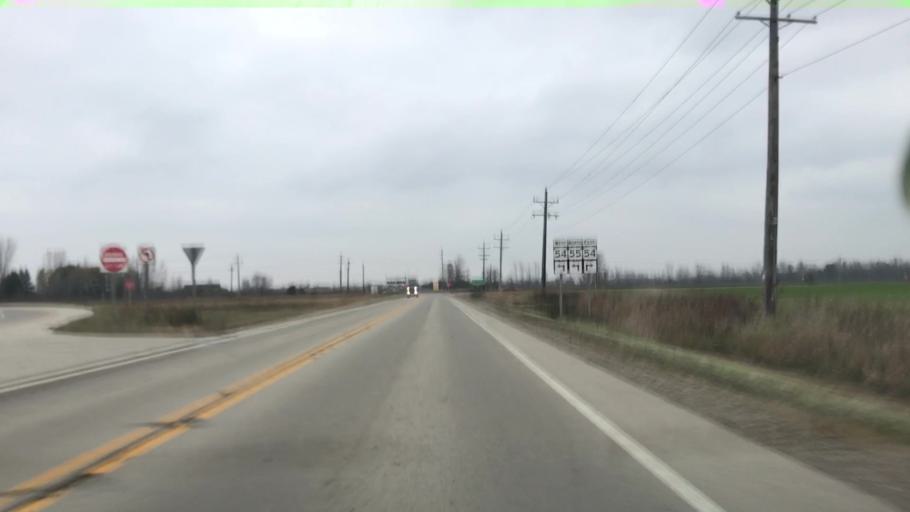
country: US
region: Wisconsin
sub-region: Outagamie County
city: Seymour
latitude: 44.4978
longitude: -88.2912
